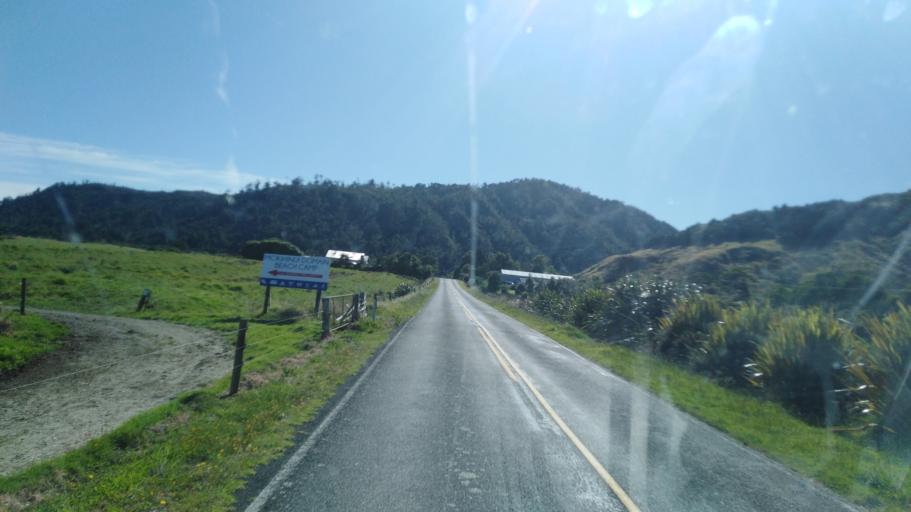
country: NZ
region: West Coast
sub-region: Buller District
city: Westport
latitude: -41.5331
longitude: 171.9375
